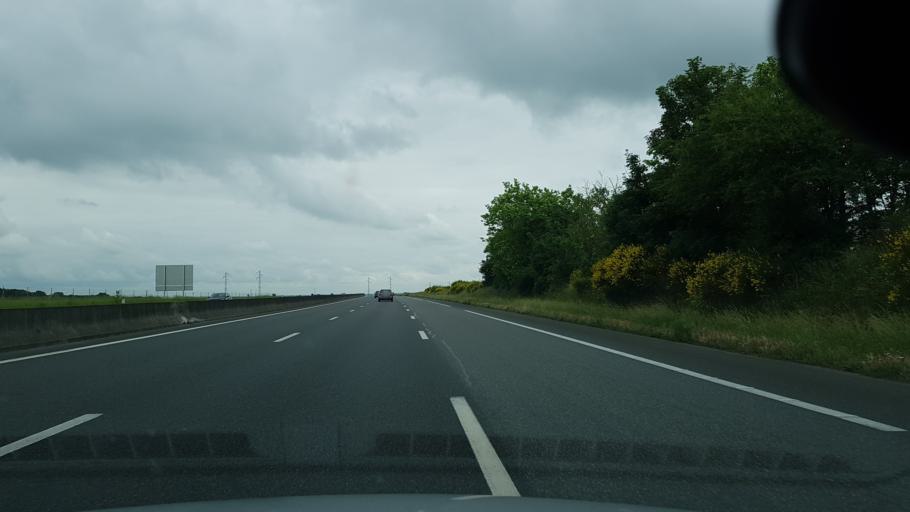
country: FR
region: Centre
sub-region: Departement du Loir-et-Cher
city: Montlivault
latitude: 47.6777
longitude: 1.4034
